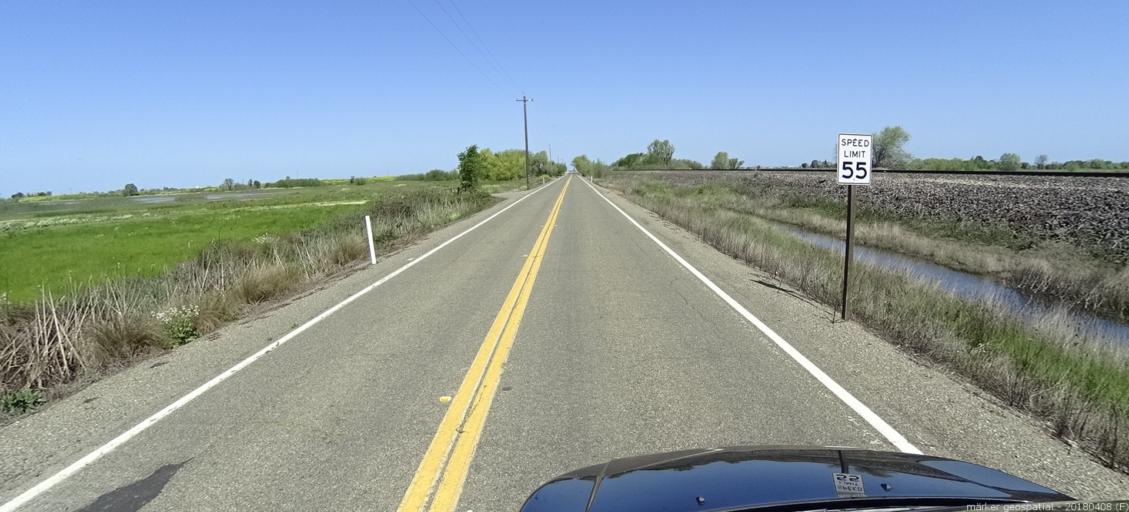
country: US
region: California
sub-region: San Joaquin County
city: Thornton
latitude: 38.2762
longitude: -121.4394
